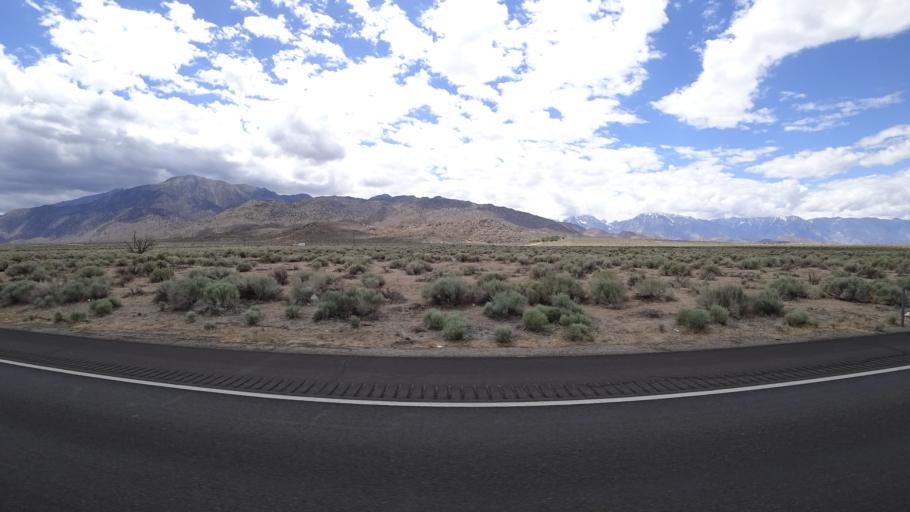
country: US
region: California
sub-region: Inyo County
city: Bishop
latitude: 37.3203
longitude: -118.3887
